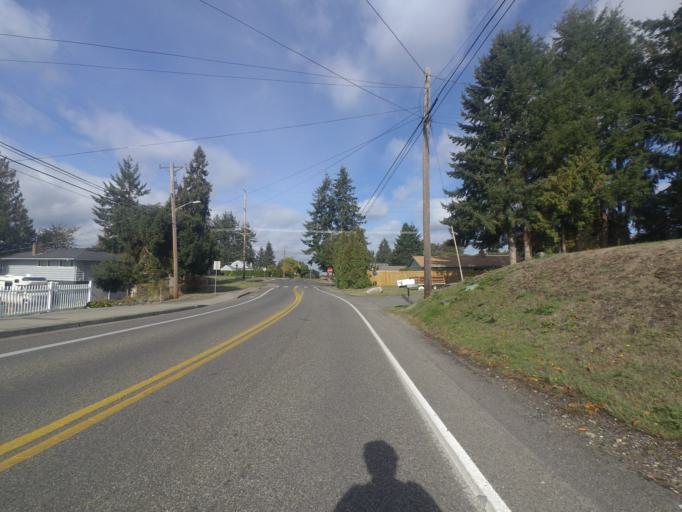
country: US
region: Washington
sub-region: Pierce County
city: University Place
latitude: 47.2275
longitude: -122.5450
